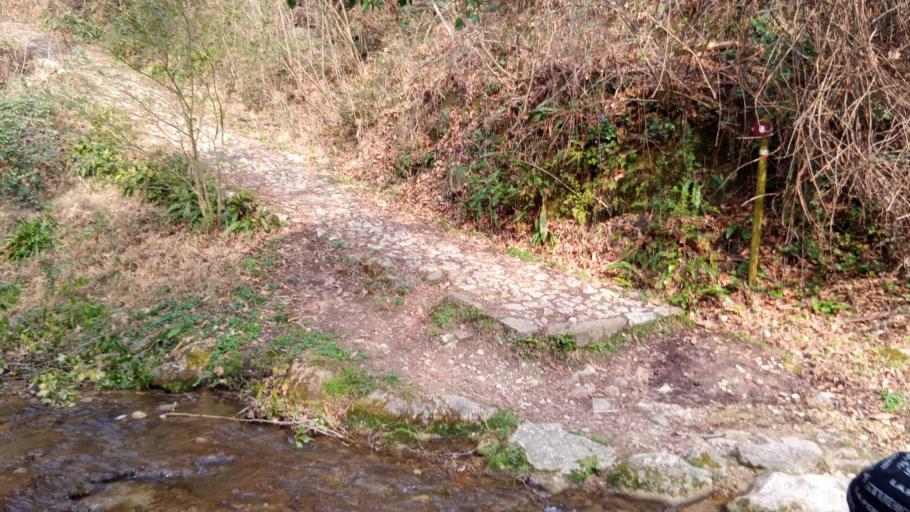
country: IT
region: Veneto
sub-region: Provincia di Vicenza
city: Campese
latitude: 45.7827
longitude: 11.6934
